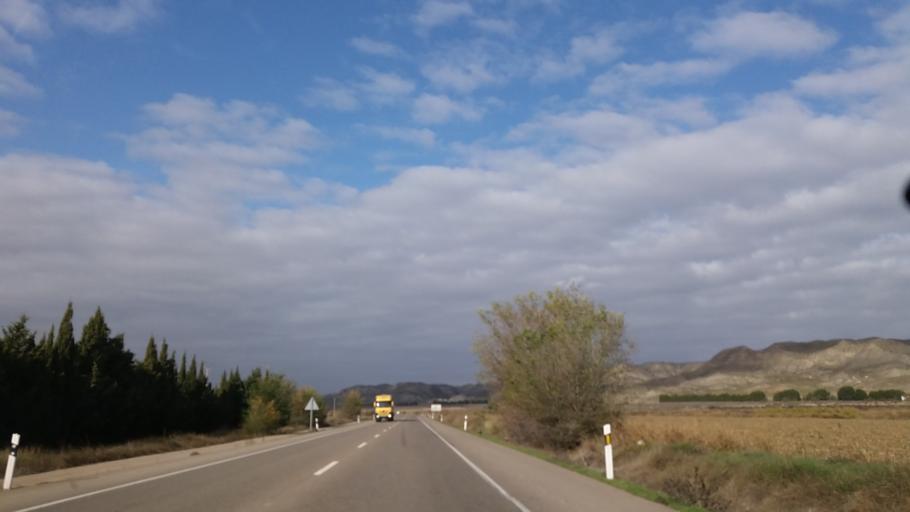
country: ES
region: Aragon
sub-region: Provincia de Zaragoza
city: Fuentes de Ebro
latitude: 41.5401
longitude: -0.5832
